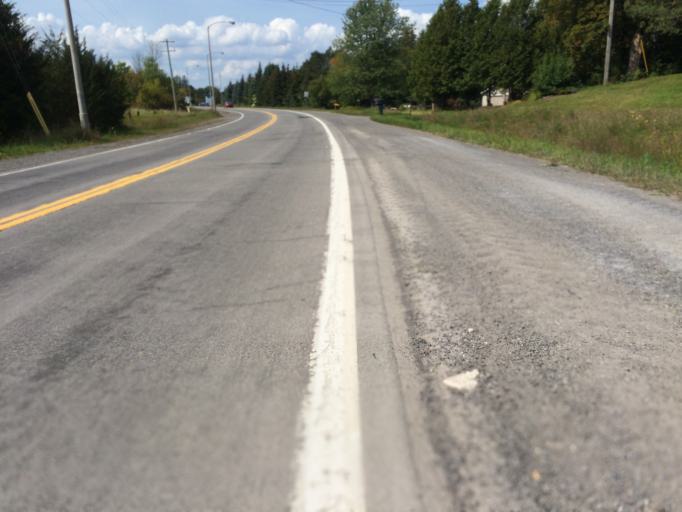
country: CA
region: Ontario
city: Bells Corners
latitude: 45.2148
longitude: -75.6660
